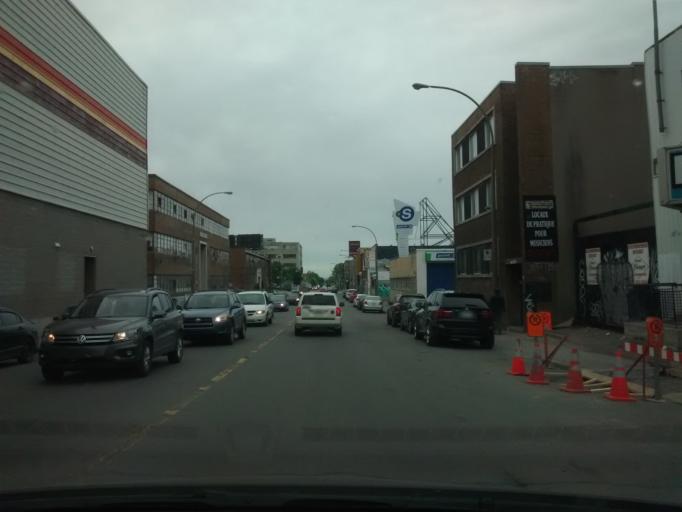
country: CA
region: Quebec
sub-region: Montreal
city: Montreal
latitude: 45.5440
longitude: -73.5805
